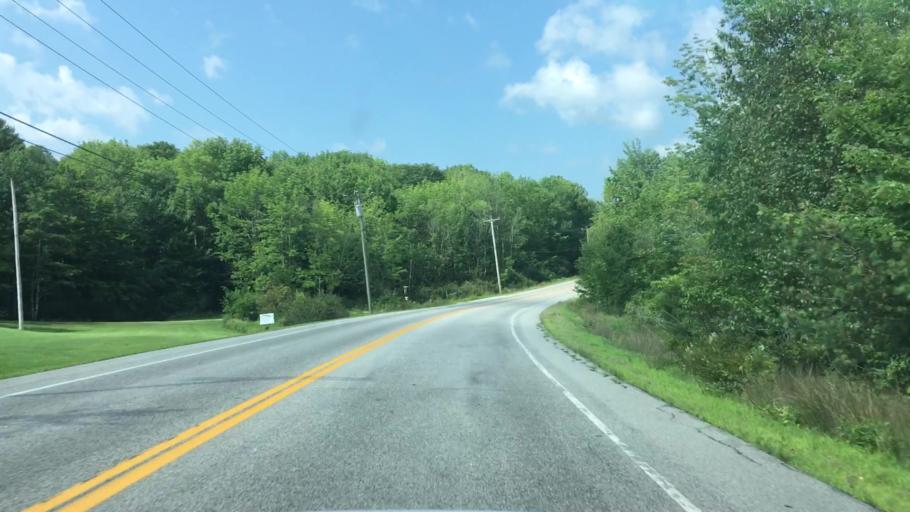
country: US
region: Maine
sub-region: Androscoggin County
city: Minot
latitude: 44.0271
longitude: -70.3152
